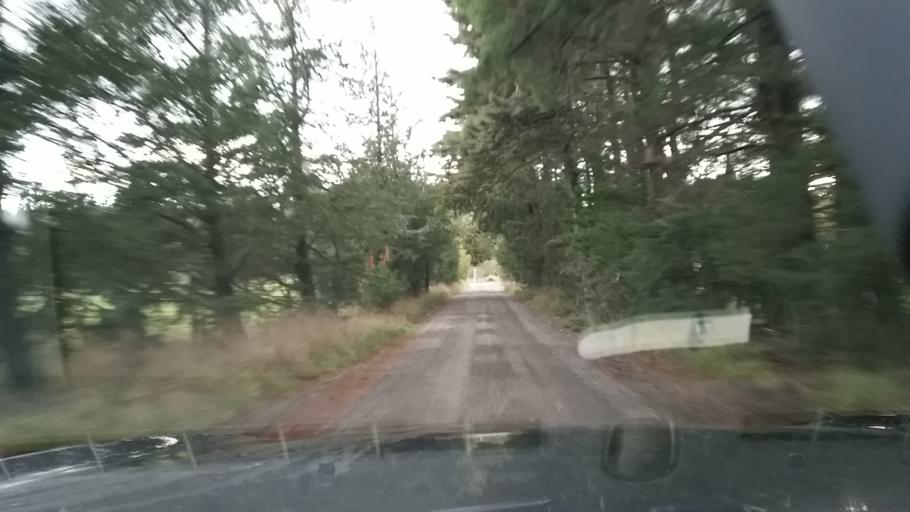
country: NZ
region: Marlborough
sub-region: Marlborough District
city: Blenheim
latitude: -41.5373
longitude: 173.6146
